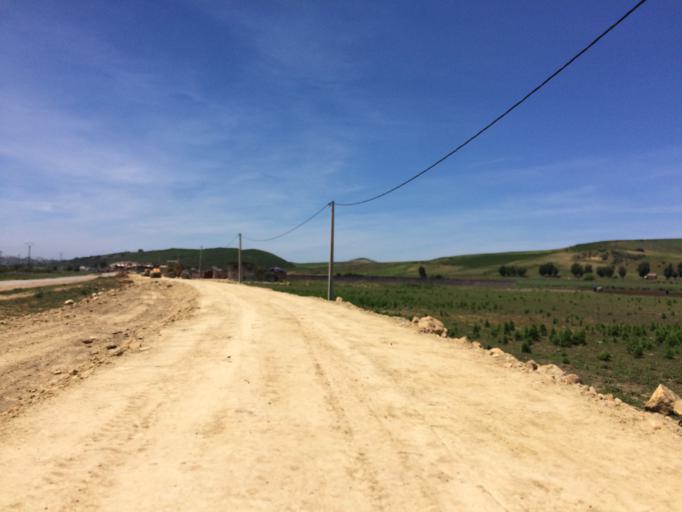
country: MA
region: Tanger-Tetouan
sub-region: Larache
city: Larache
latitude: 35.2016
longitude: -6.0874
